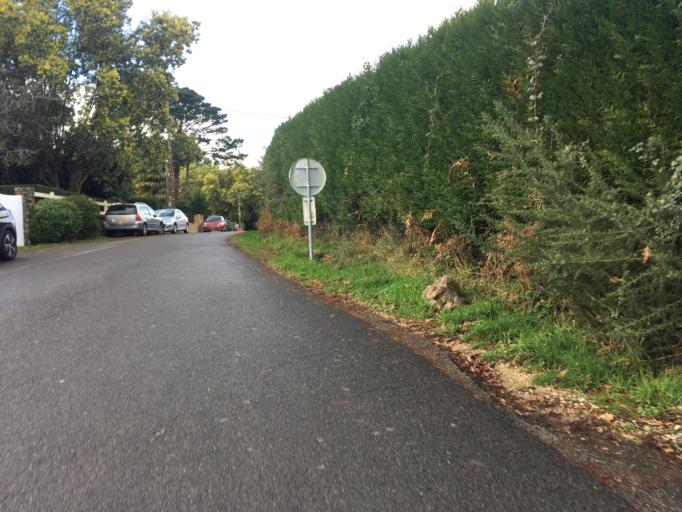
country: FR
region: Brittany
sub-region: Departement du Morbihan
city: Larmor-Baden
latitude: 47.5993
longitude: -2.8623
